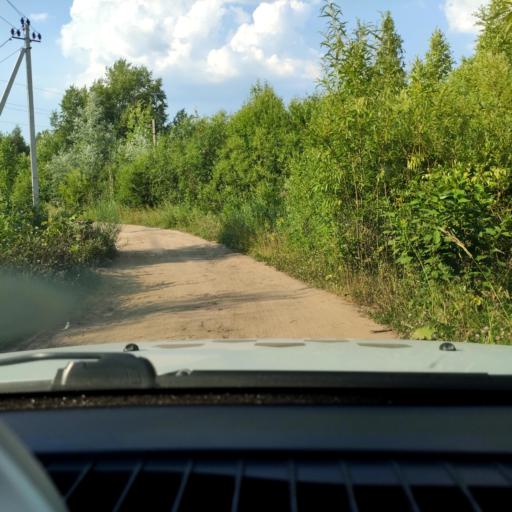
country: RU
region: Perm
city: Perm
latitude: 58.0236
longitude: 56.2114
